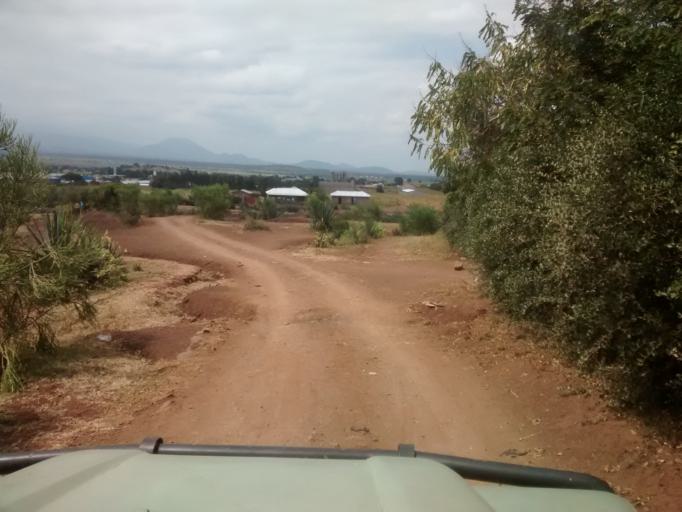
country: TZ
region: Arusha
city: Arusha
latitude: -3.3922
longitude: 36.5900
